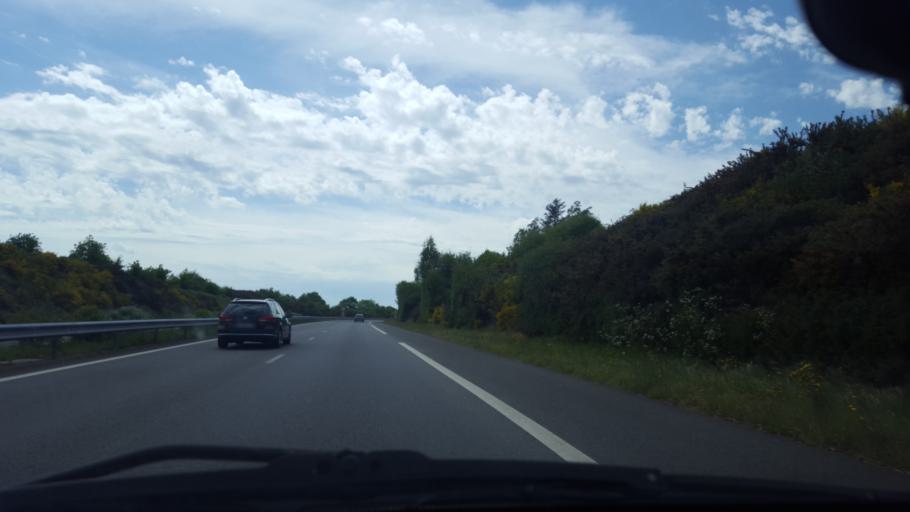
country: FR
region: Pays de la Loire
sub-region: Departement de la Loire-Atlantique
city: Saint-Philbert-de-Grand-Lieu
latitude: 47.0295
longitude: -1.6660
